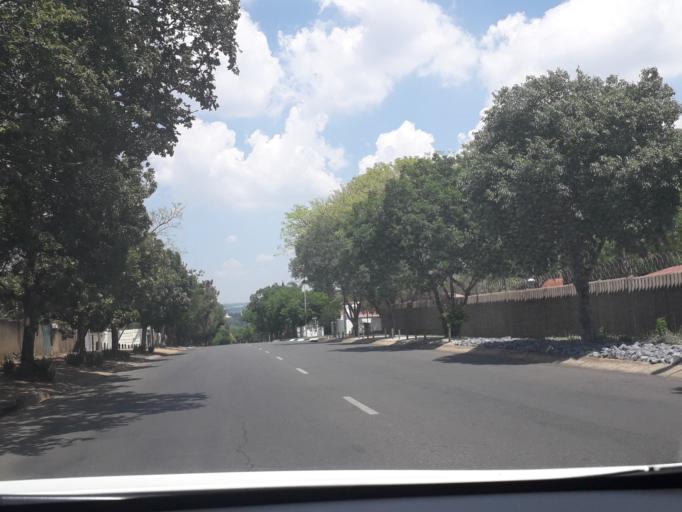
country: ZA
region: Gauteng
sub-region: City of Johannesburg Metropolitan Municipality
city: Midrand
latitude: -26.0384
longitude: 28.0777
